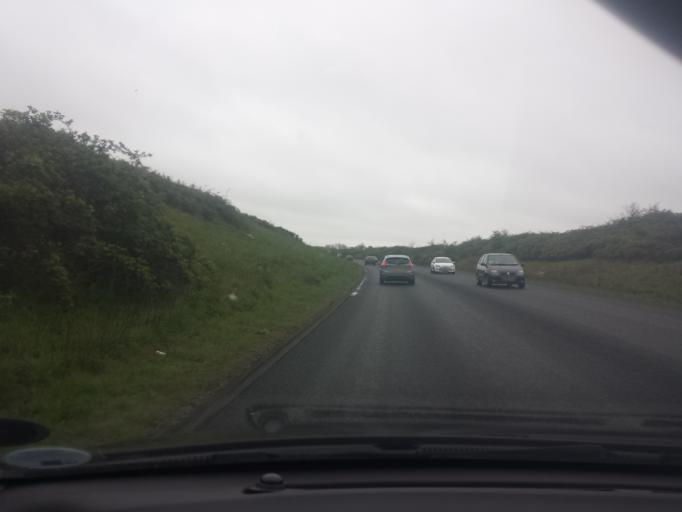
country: GB
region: England
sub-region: Essex
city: Little Clacton
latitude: 51.8417
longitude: 1.1134
